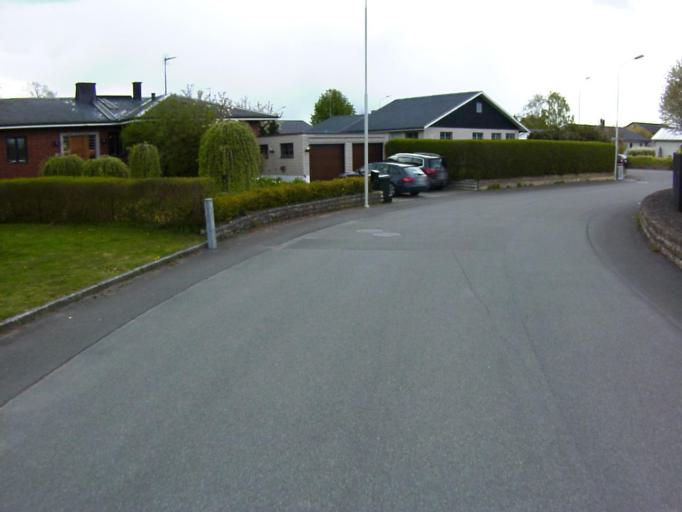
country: SE
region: Skane
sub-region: Kristianstads Kommun
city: Kristianstad
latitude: 56.0474
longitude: 14.1777
